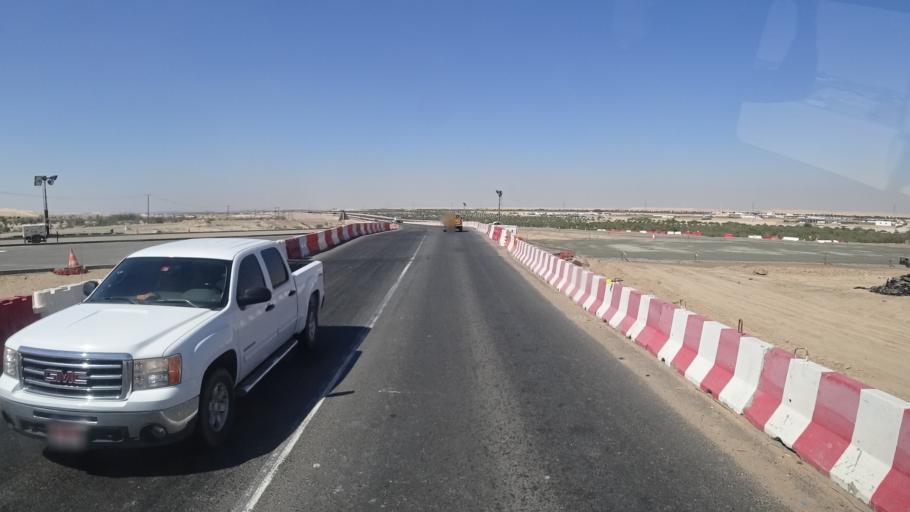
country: AE
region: Abu Dhabi
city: Abu Dhabi
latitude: 24.2018
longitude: 54.8577
